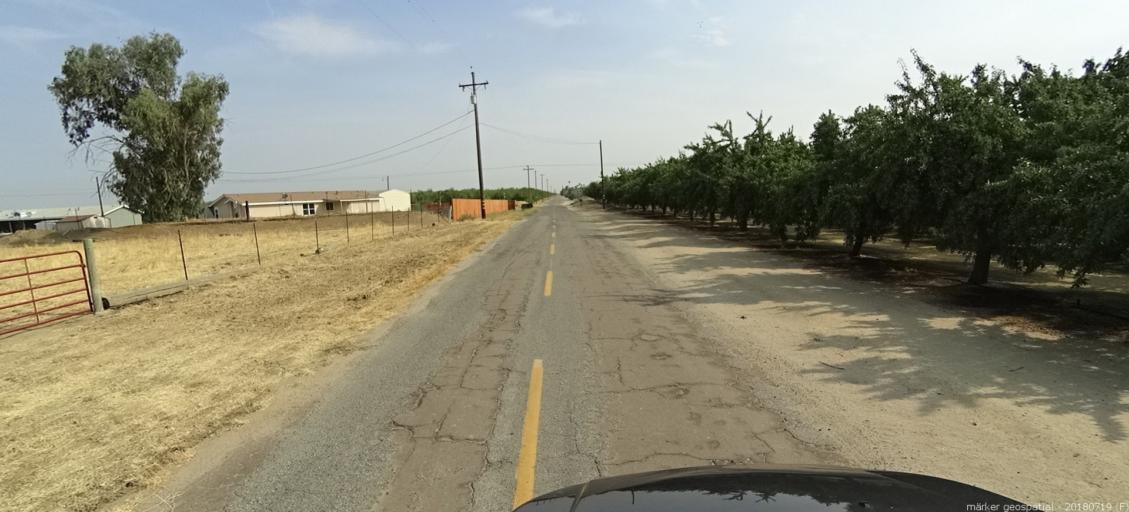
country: US
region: California
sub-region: Madera County
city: Fairmead
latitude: 37.0679
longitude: -120.1750
